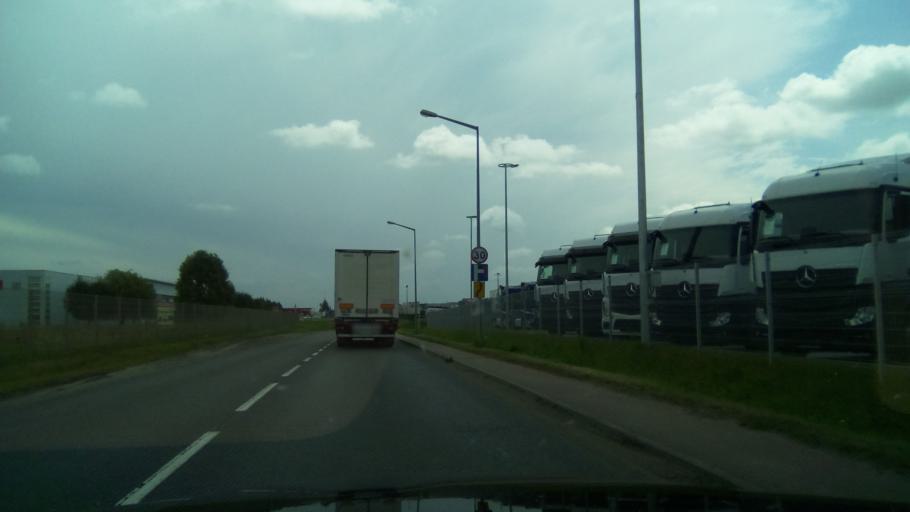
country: PL
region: Greater Poland Voivodeship
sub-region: Powiat poznanski
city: Komorniki
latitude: 52.3482
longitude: 16.8246
